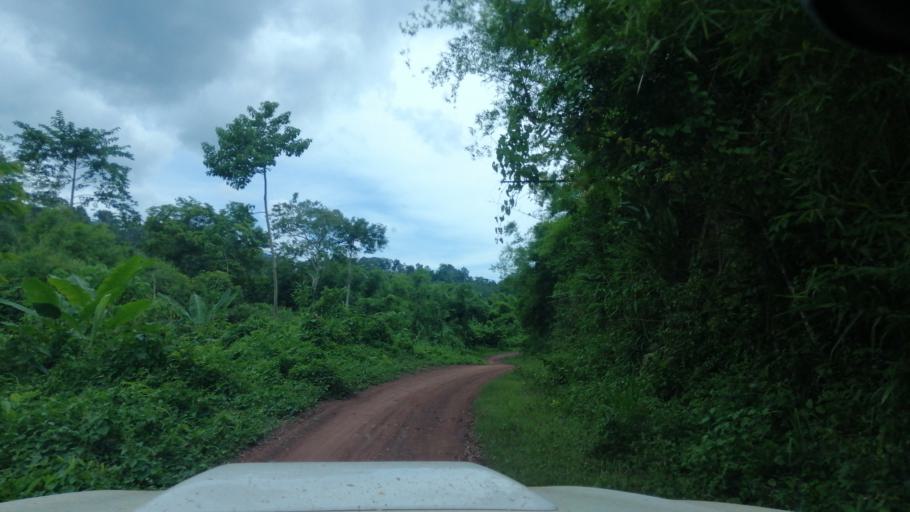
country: TH
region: Nan
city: Mae Charim
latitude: 18.7681
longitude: 101.3104
